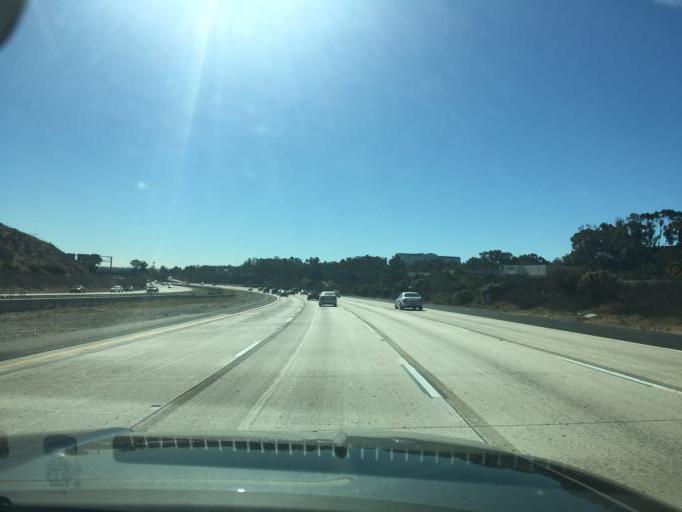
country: US
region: California
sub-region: San Diego County
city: La Mesa
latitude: 32.8414
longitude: -117.1210
